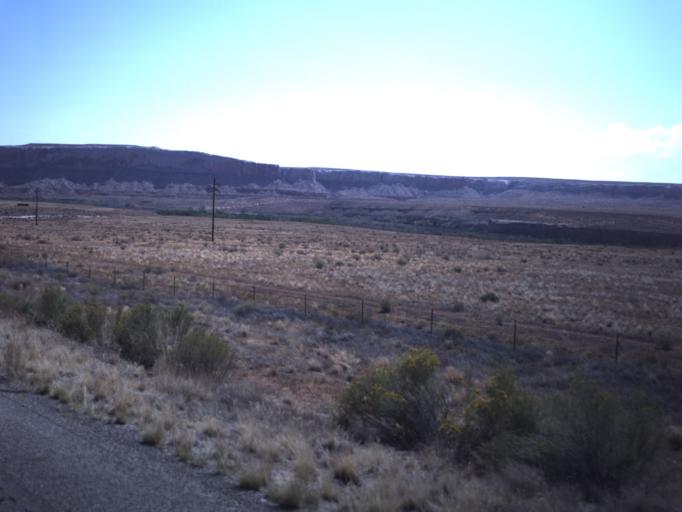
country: US
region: Utah
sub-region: San Juan County
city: Blanding
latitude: 37.2659
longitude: -109.6213
